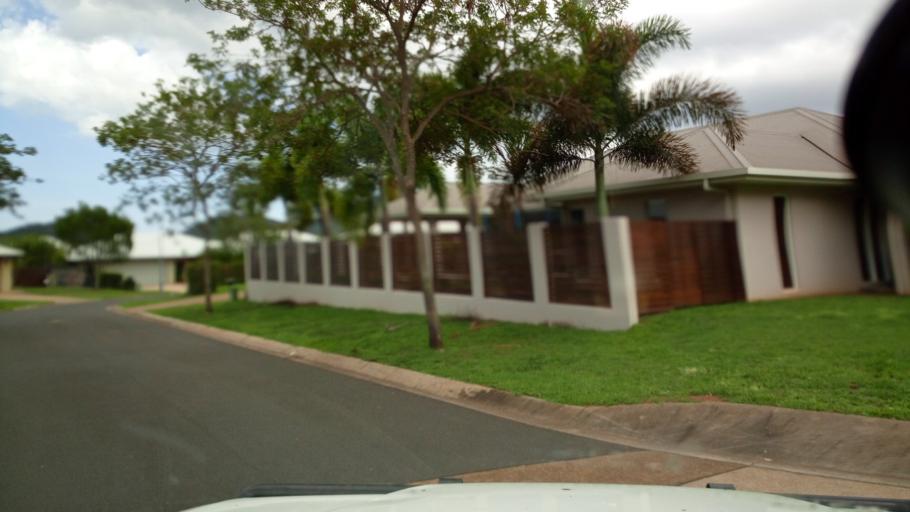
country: AU
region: Queensland
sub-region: Cairns
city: Redlynch
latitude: -16.8992
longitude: 145.6948
